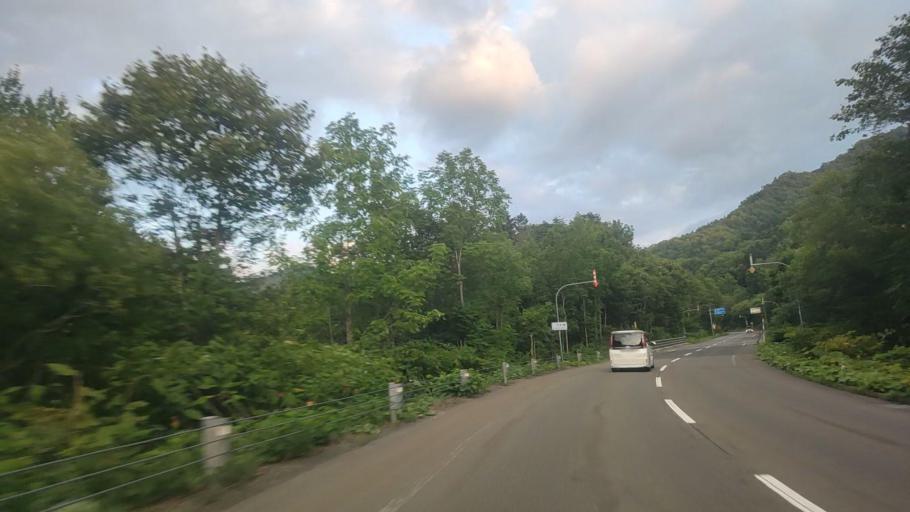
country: JP
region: Hokkaido
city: Ashibetsu
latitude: 43.3682
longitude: 142.2279
